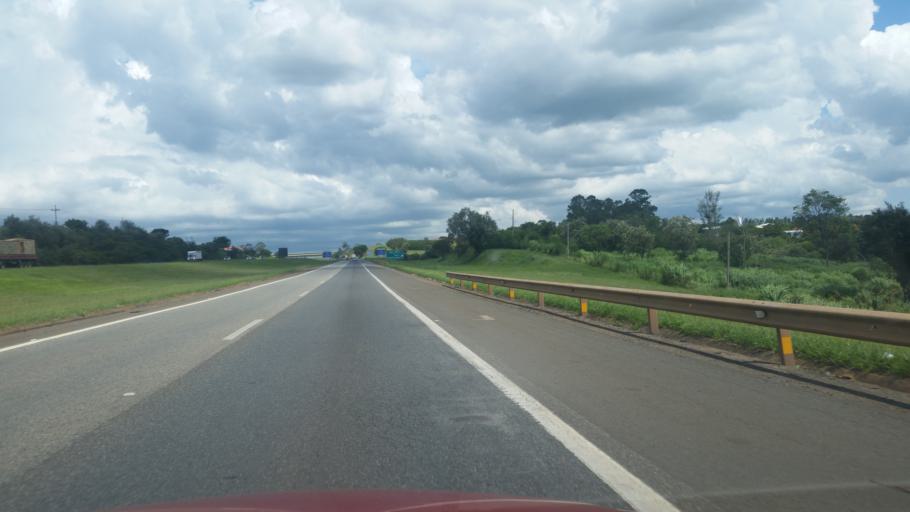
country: BR
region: Sao Paulo
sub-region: Tatui
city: Tatui
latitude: -23.2800
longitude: -47.8157
